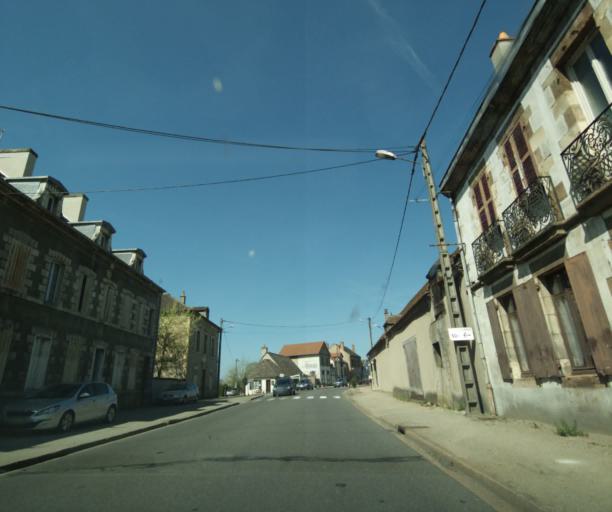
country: FR
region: Auvergne
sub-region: Departement de l'Allier
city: Trevol
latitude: 46.6596
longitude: 3.2482
